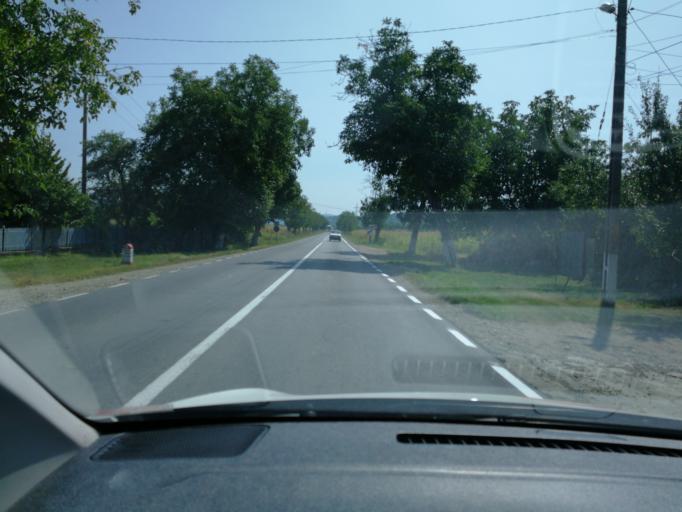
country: RO
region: Prahova
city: Drajna de Jos
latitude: 45.2348
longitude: 26.0293
